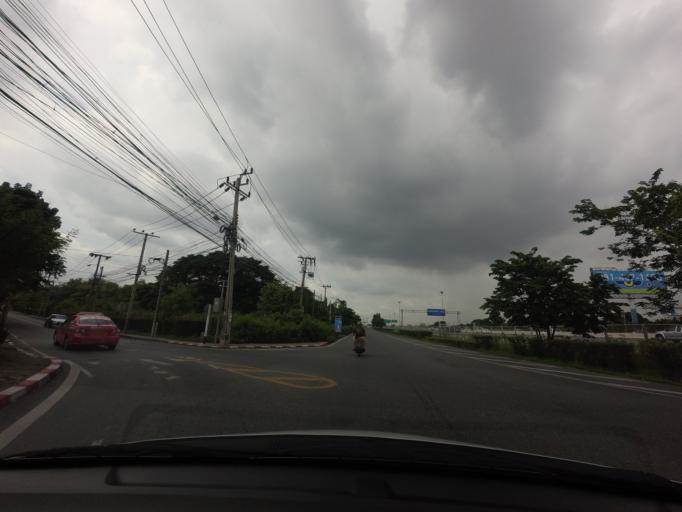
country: TH
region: Bangkok
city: Saphan Sung
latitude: 13.7685
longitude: 100.6918
